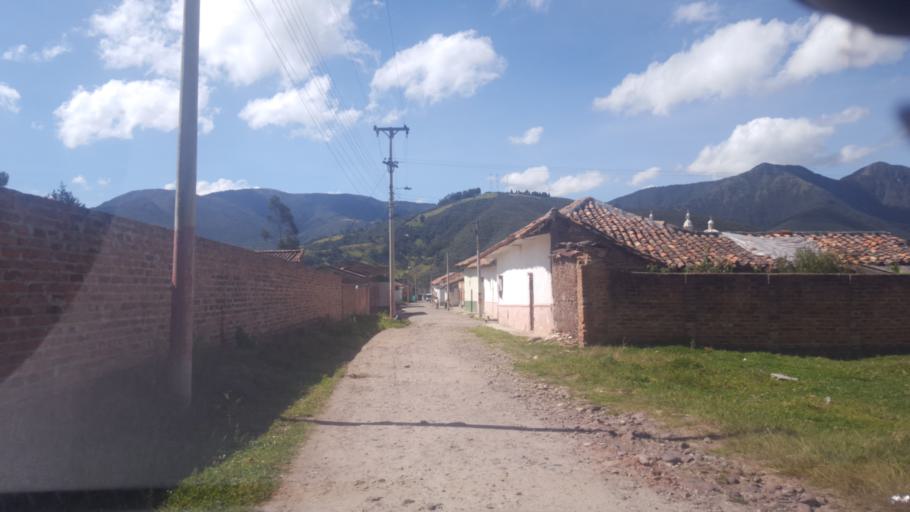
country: CO
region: Boyaca
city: Belen
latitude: 5.9931
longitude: -72.9138
